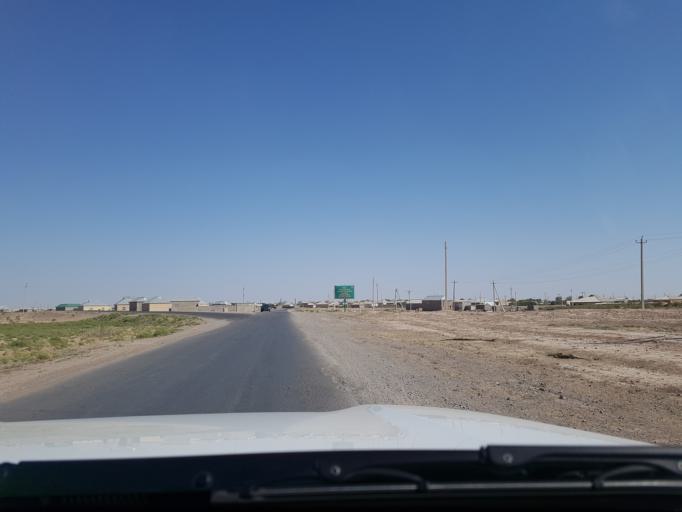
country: IR
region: Razavi Khorasan
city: Sarakhs
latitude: 36.5210
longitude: 61.2476
